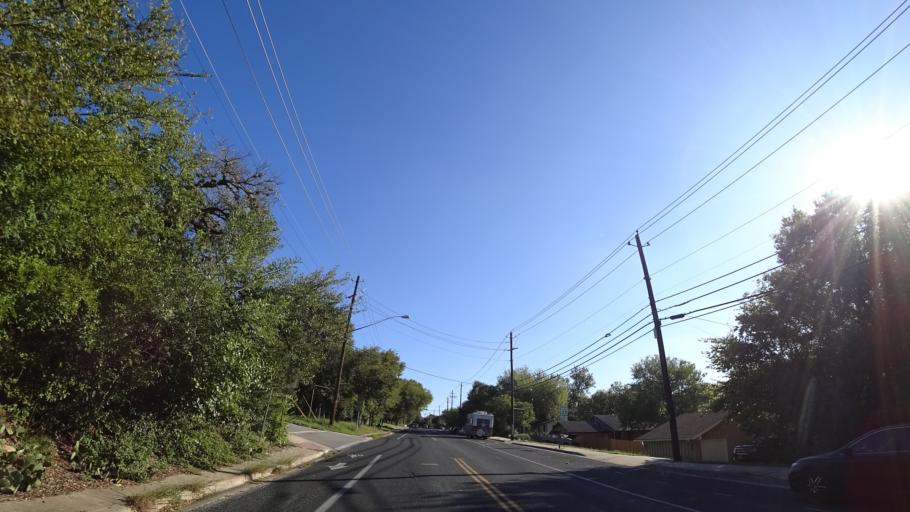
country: US
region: Texas
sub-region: Travis County
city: Austin
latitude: 30.2239
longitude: -97.7348
